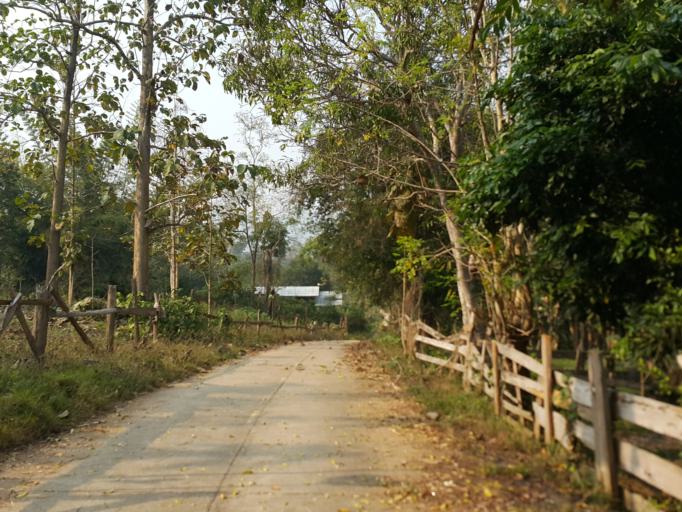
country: TH
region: Lamphun
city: Li
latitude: 17.6037
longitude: 98.9640
